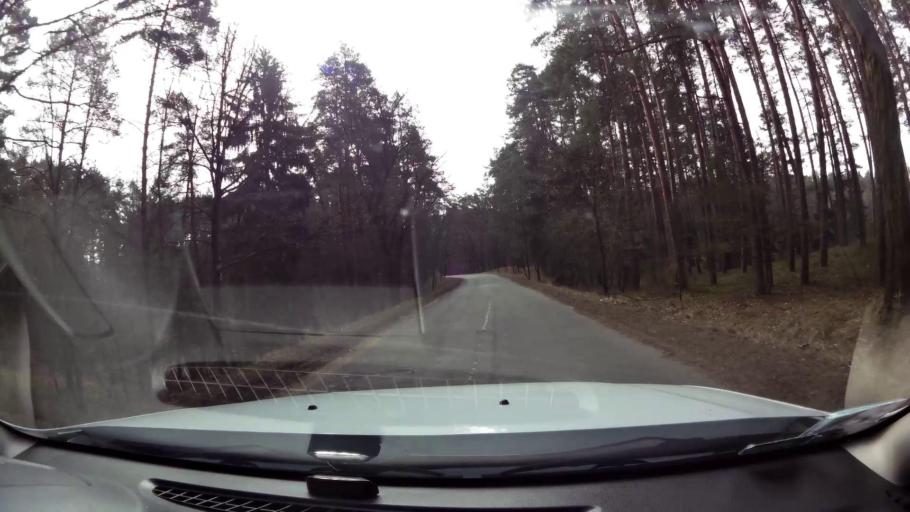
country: PL
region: West Pomeranian Voivodeship
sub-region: Powiat mysliborski
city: Debno
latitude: 52.8192
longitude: 14.6358
